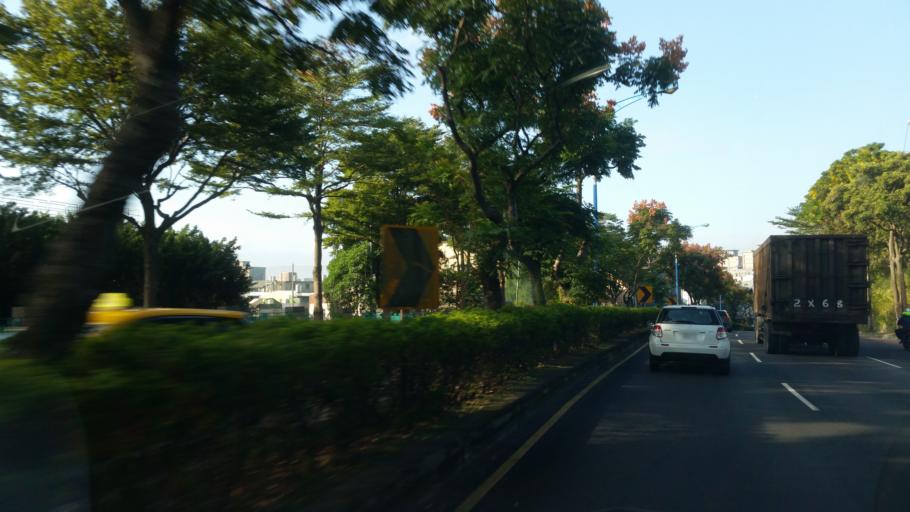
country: TW
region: Taiwan
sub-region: Taoyuan
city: Taoyuan
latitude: 24.9985
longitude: 121.3377
